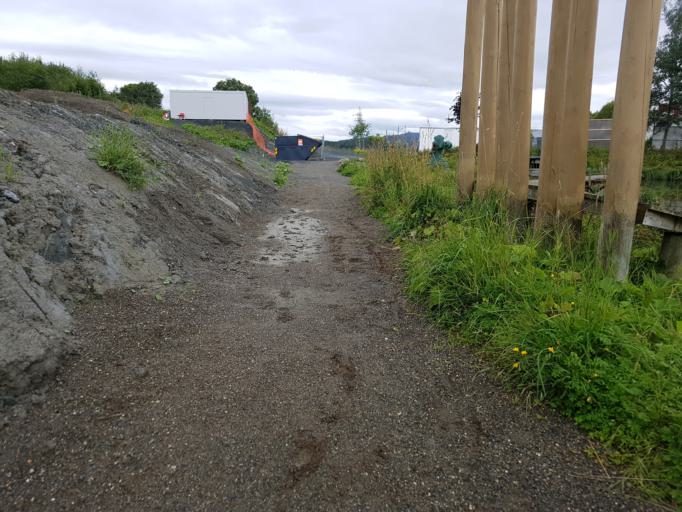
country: NO
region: Sor-Trondelag
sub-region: Trondheim
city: Trondheim
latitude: 63.3891
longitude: 10.4355
